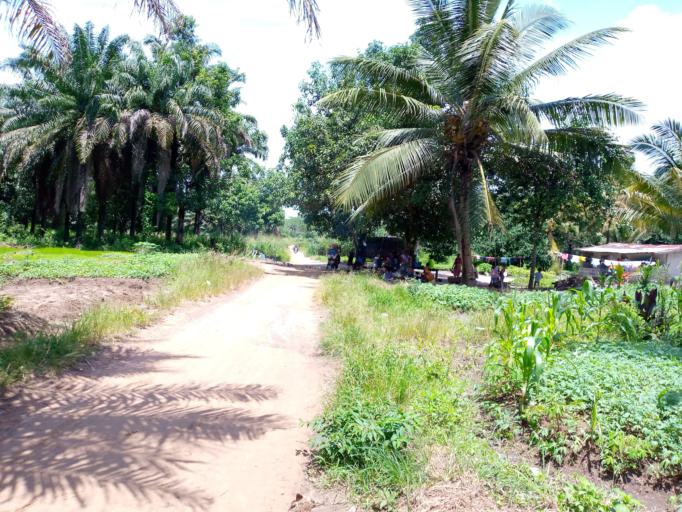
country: SL
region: Northern Province
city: Magburaka
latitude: 8.7087
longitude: -11.9595
